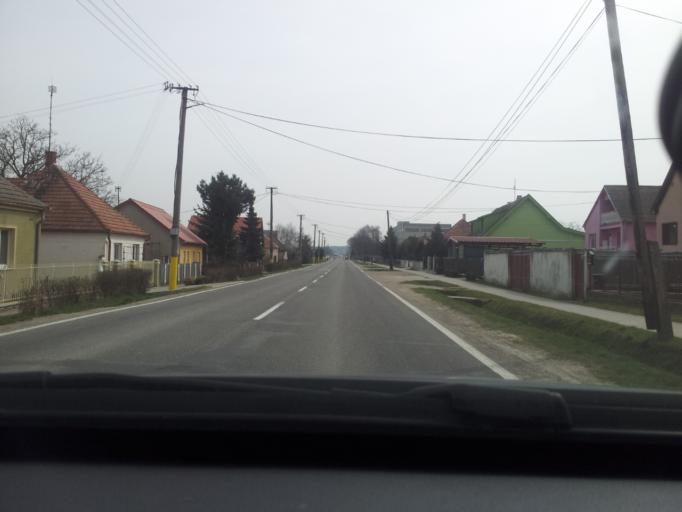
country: SK
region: Trnavsky
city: Hlohovec
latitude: 48.3648
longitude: 17.9056
